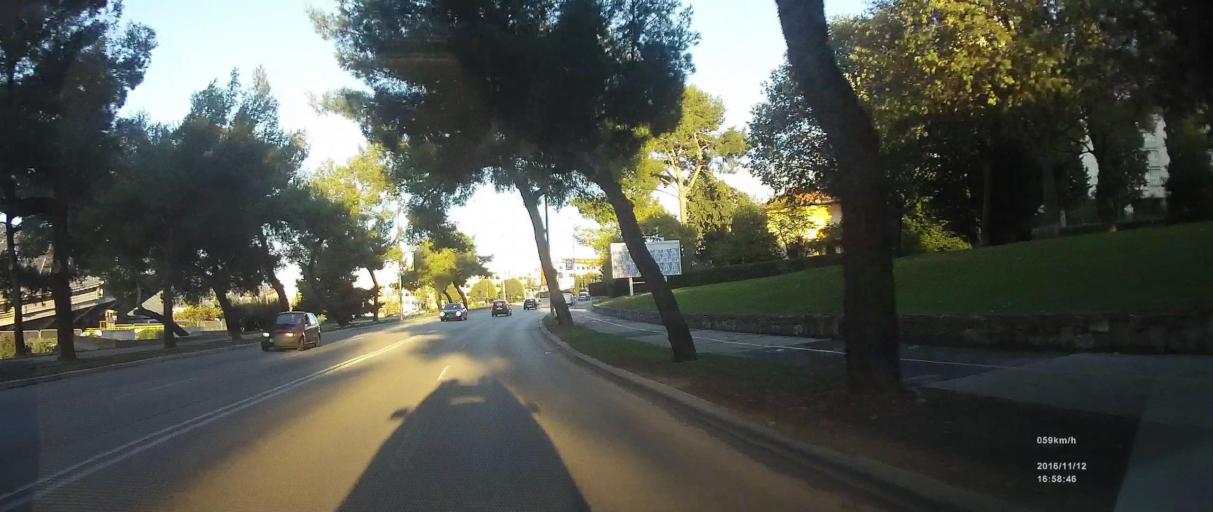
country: HR
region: Splitsko-Dalmatinska
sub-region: Grad Split
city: Split
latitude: 43.5177
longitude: 16.4318
